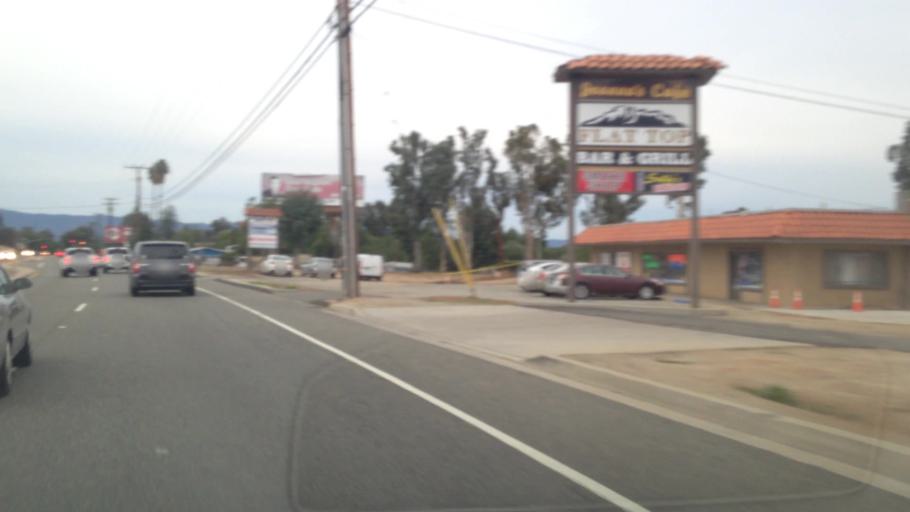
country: US
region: California
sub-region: Riverside County
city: Woodcrest
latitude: 33.8860
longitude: -117.3490
